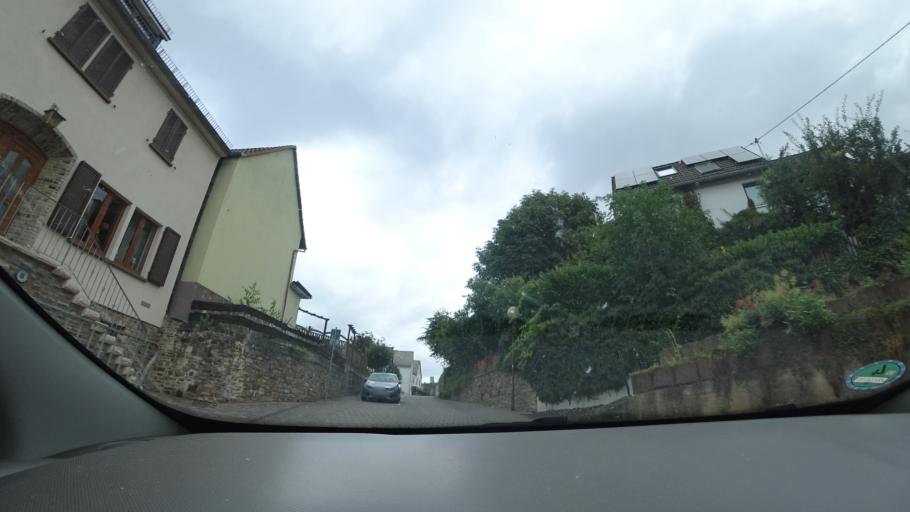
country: DE
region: Rheinland-Pfalz
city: Hillscheid
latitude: 50.4057
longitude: 7.6978
